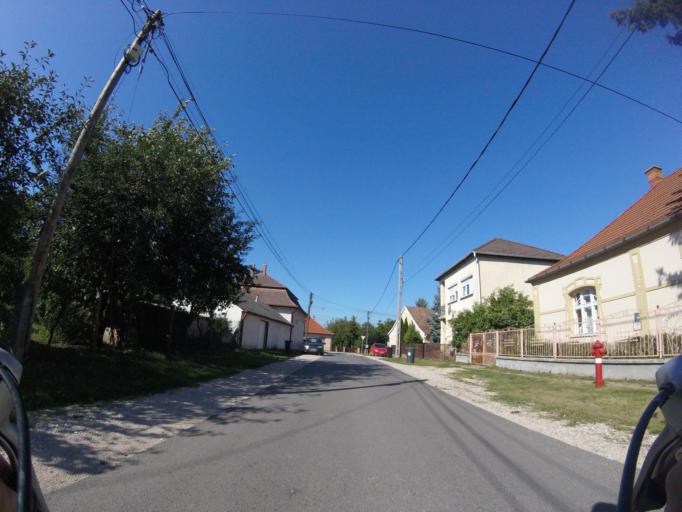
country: HU
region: Pest
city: Biatorbagy
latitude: 47.4720
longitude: 18.8250
